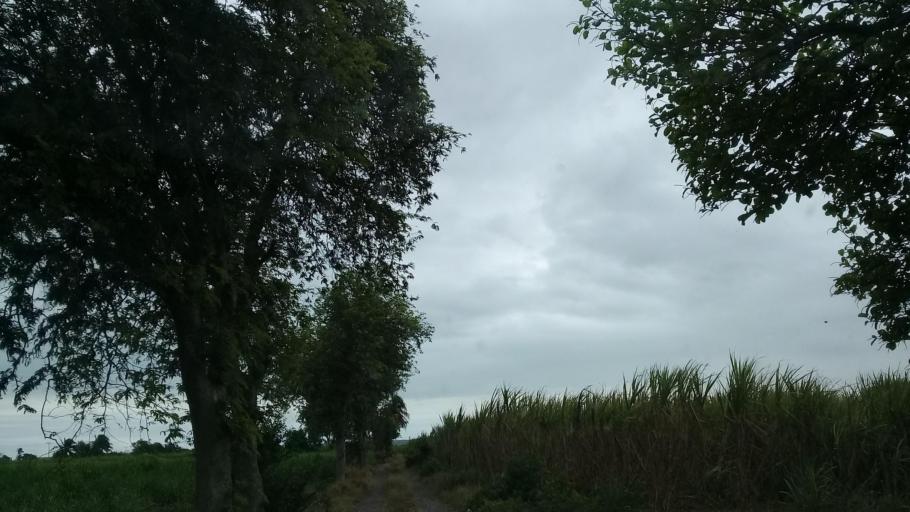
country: MX
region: Veracruz
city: Ursulo Galvan
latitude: 19.3832
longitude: -96.3601
